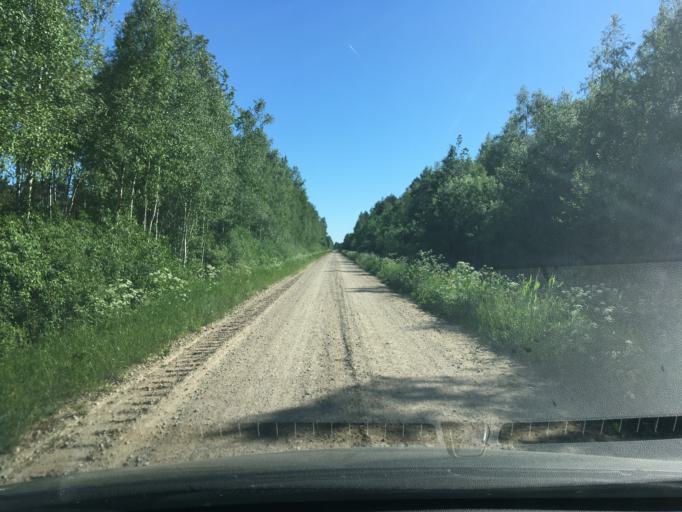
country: EE
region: Laeaene
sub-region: Lihula vald
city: Lihula
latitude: 58.6390
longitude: 23.7621
